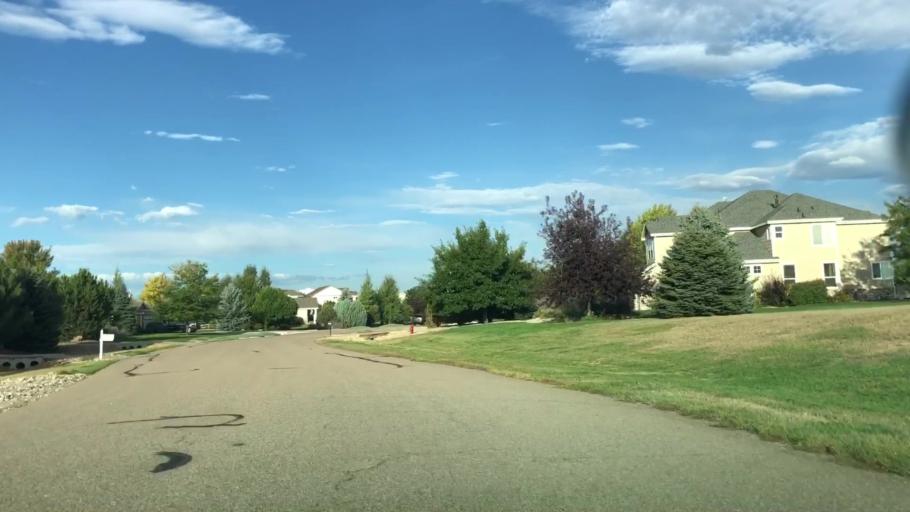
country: US
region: Colorado
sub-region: Weld County
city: Windsor
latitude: 40.4377
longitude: -104.9582
